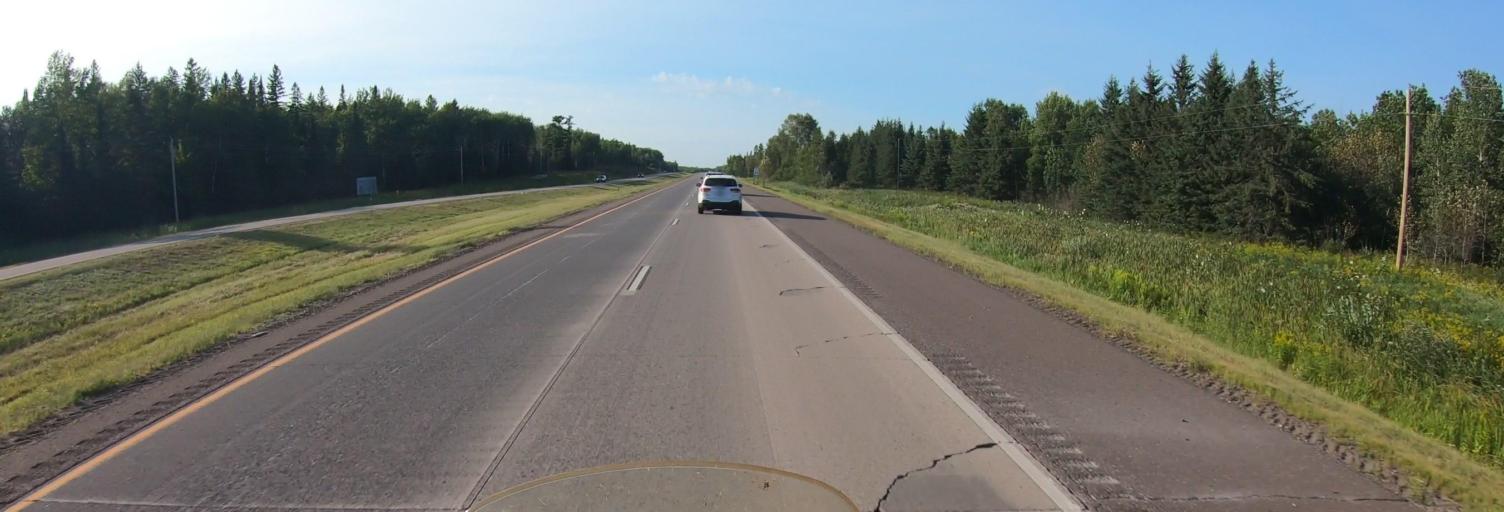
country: US
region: Minnesota
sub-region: Carlton County
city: Cloquet
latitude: 46.9633
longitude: -92.4626
